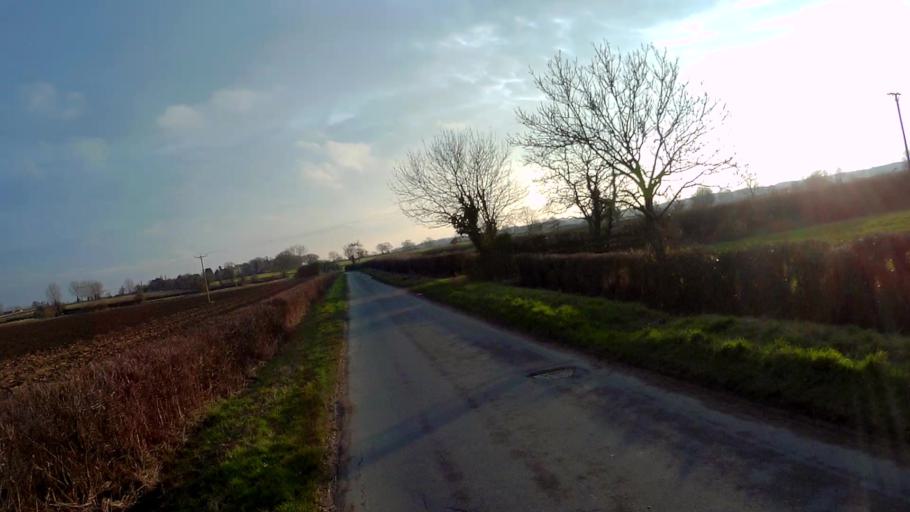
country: GB
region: England
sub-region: Lincolnshire
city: Bourne
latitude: 52.8100
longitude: -0.3979
